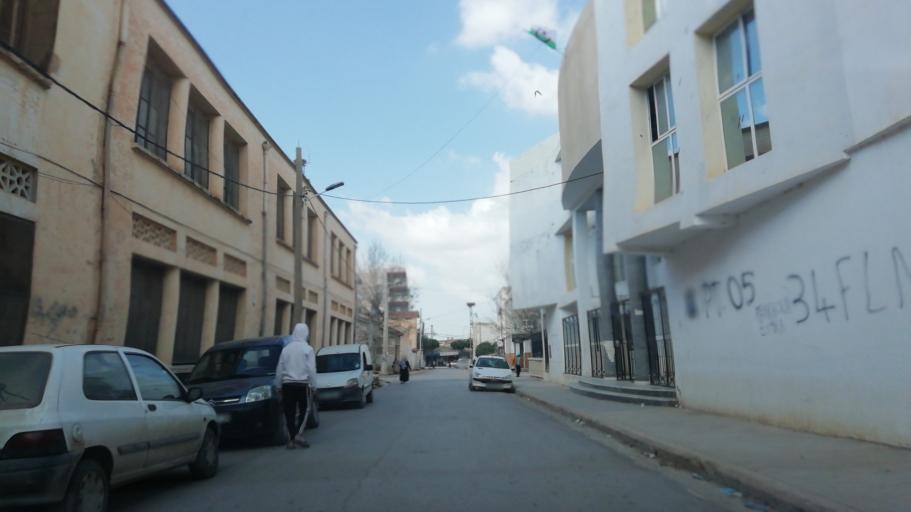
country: DZ
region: Mascara
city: Mascara
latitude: 35.5863
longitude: 0.0691
